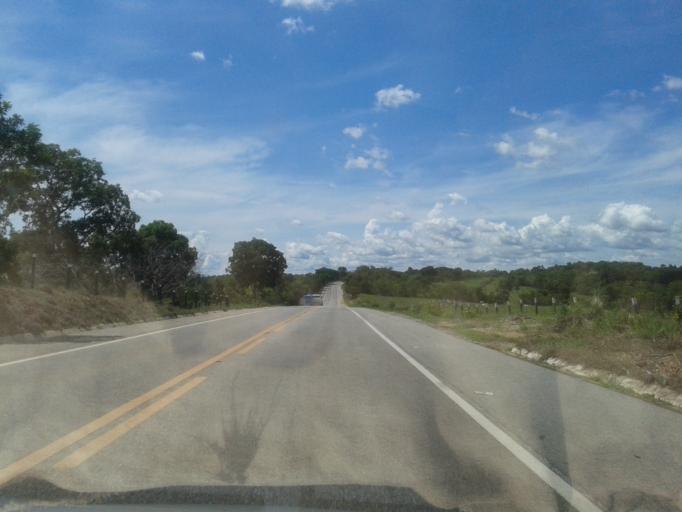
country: BR
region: Goias
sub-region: Goias
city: Goias
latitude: -15.7435
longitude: -50.1783
